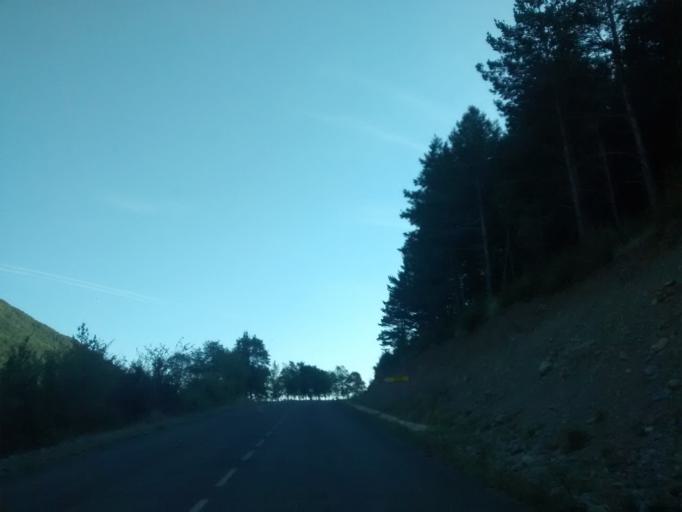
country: ES
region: Aragon
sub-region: Provincia de Huesca
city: Anso
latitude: 42.7664
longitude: -0.7448
